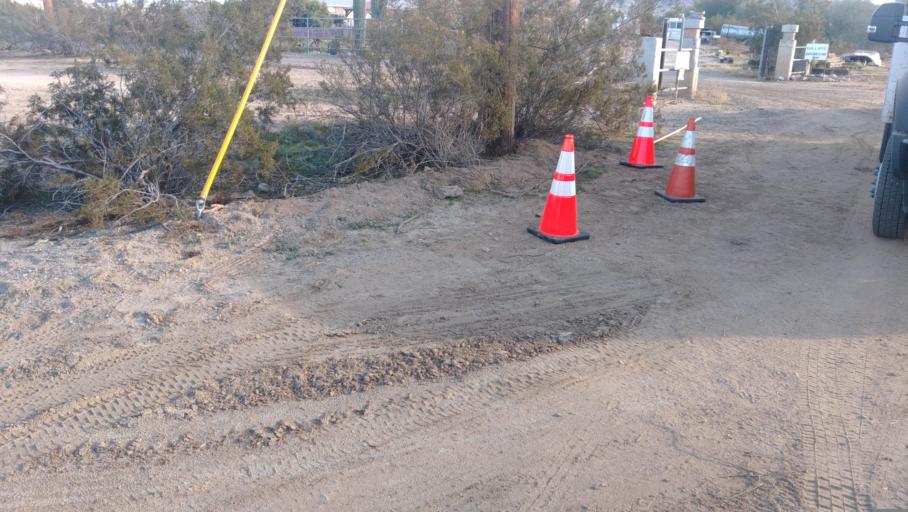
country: US
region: Arizona
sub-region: Maricopa County
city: Queen Creek
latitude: 33.2187
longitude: -111.6646
